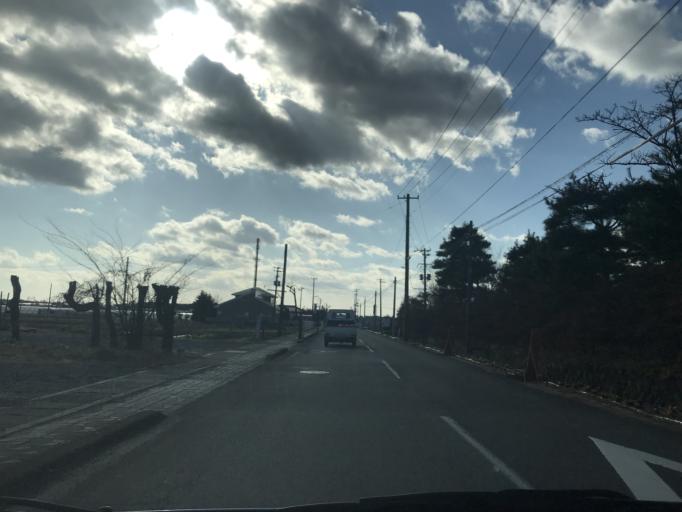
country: JP
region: Iwate
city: Ichinoseki
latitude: 38.7531
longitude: 141.0665
